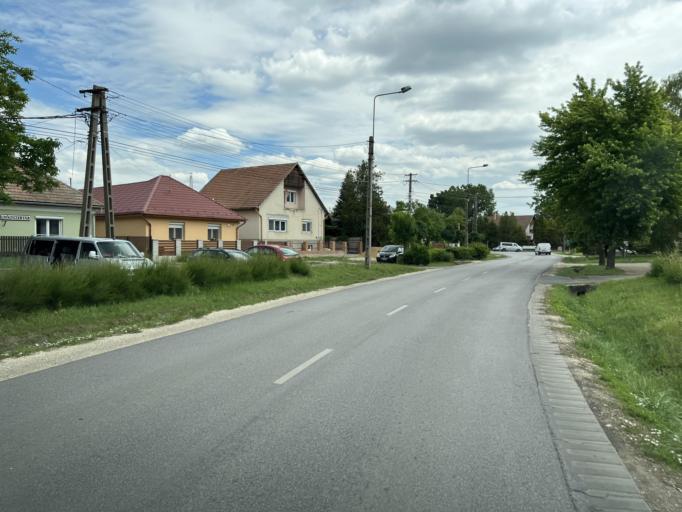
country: HU
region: Pest
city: Koka
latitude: 47.4891
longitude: 19.5808
